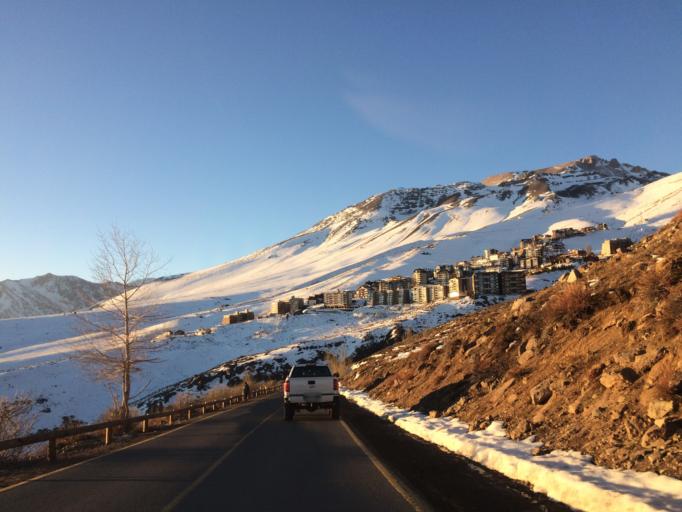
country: CL
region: Santiago Metropolitan
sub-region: Provincia de Santiago
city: Villa Presidente Frei, Nunoa, Santiago, Chile
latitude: -33.3424
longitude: -70.2947
